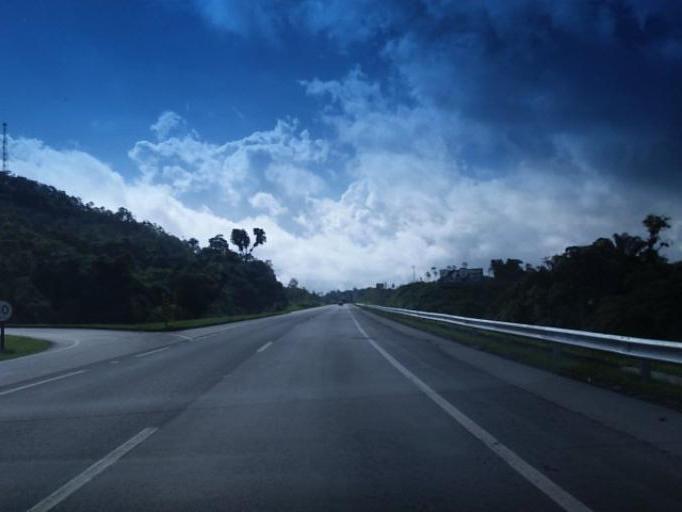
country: BR
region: Parana
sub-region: Antonina
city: Antonina
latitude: -25.1107
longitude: -48.7554
